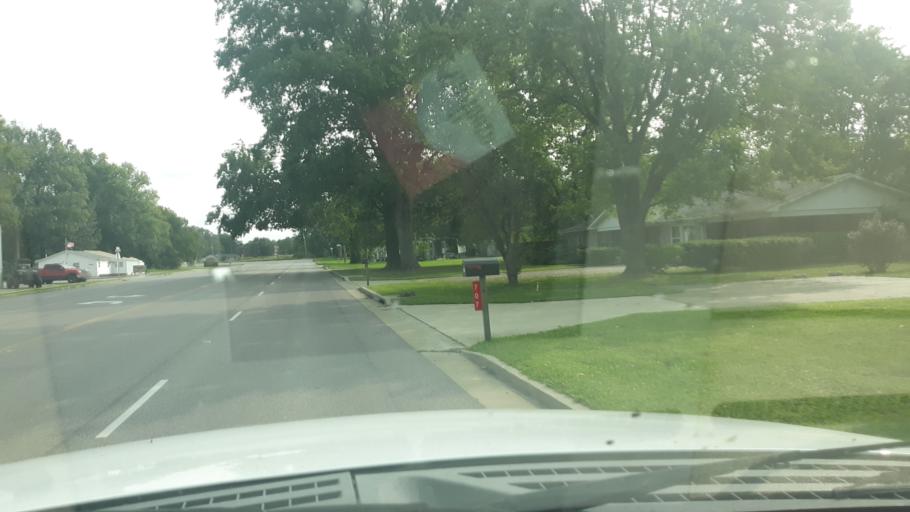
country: US
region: Illinois
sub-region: Saline County
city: Eldorado
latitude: 37.8097
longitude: -88.4314
